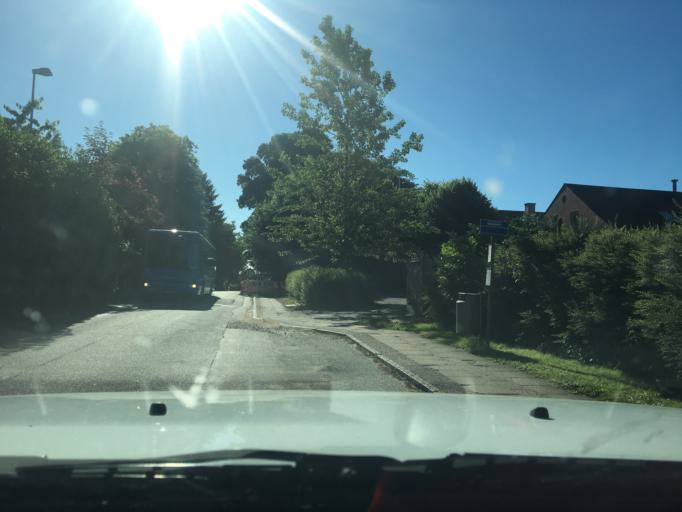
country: DK
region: Central Jutland
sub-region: Syddjurs Kommune
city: Hornslet
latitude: 56.3214
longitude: 10.3046
